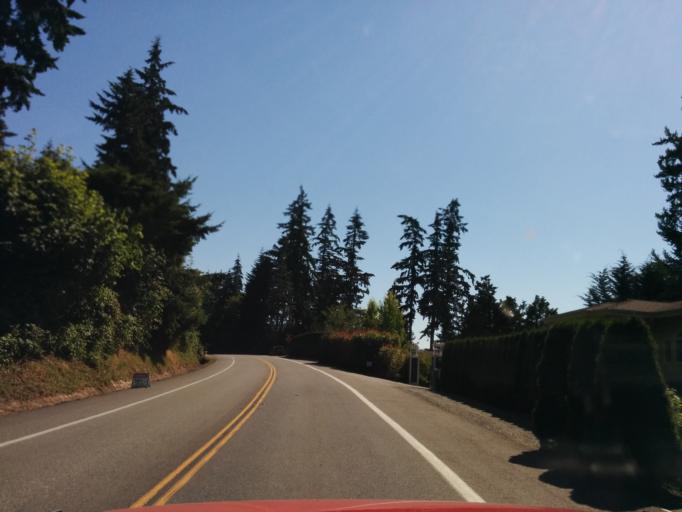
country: US
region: Washington
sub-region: King County
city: West Lake Sammamish
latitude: 47.5922
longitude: -122.0845
